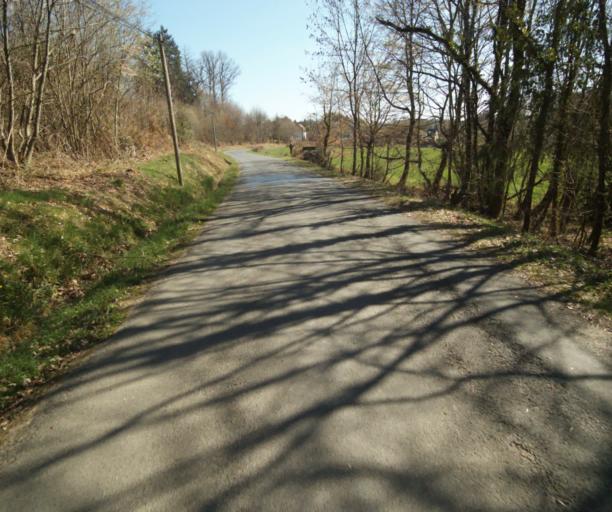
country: FR
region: Limousin
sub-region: Departement de la Correze
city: Saint-Mexant
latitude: 45.2957
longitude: 1.6845
